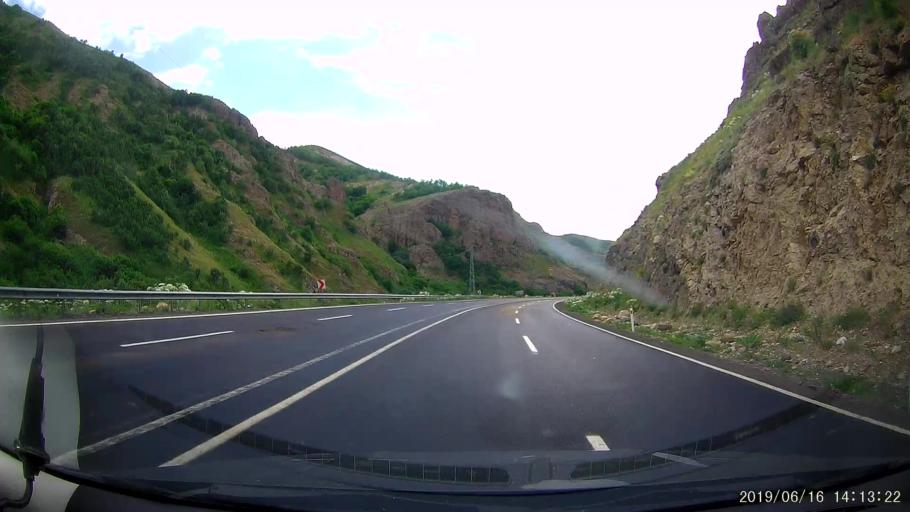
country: TR
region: Agri
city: Tahir
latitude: 39.7972
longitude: 42.5182
